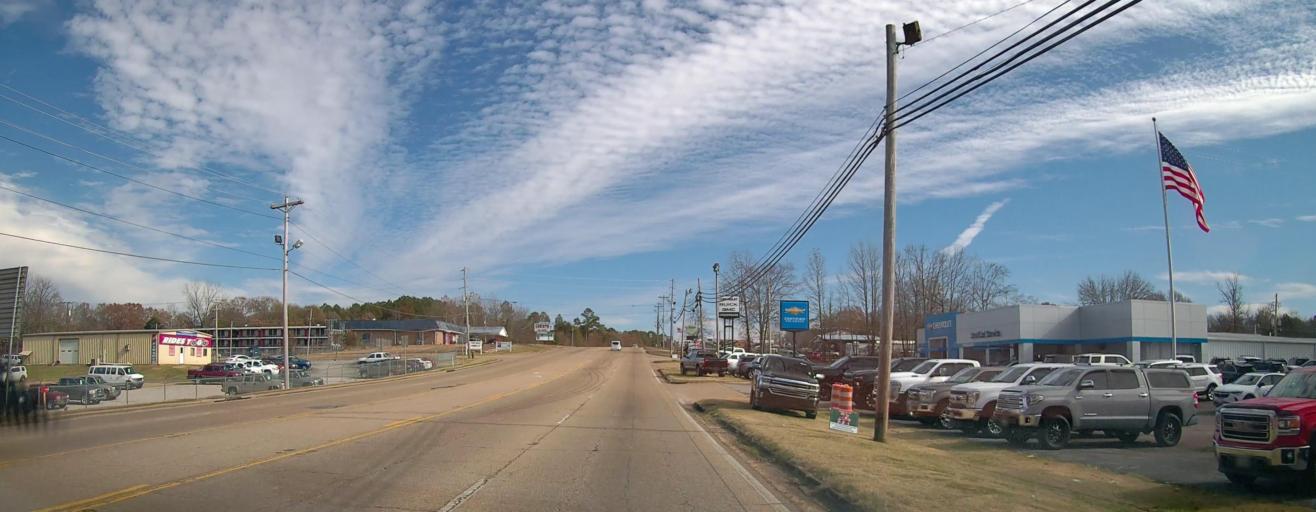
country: US
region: Mississippi
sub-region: Alcorn County
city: Corinth
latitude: 34.9306
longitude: -88.5426
